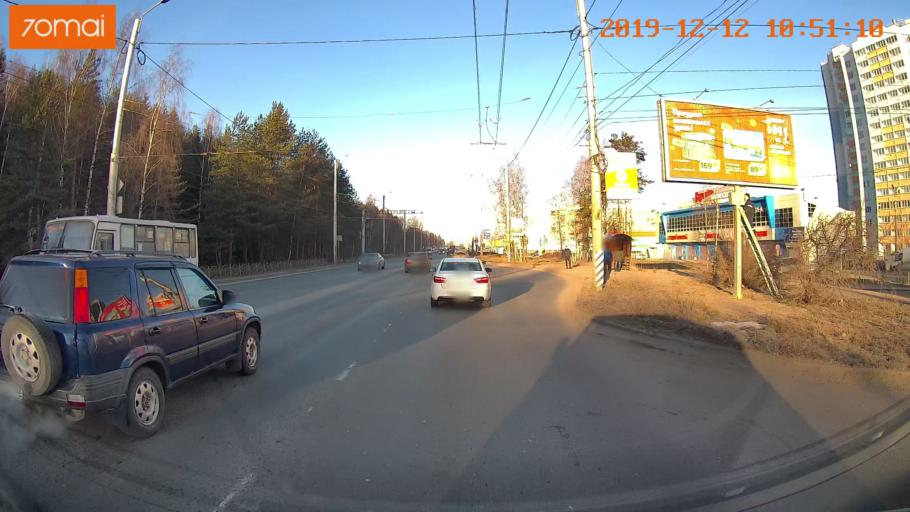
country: RU
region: Ivanovo
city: Kokhma
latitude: 56.9519
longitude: 41.0458
